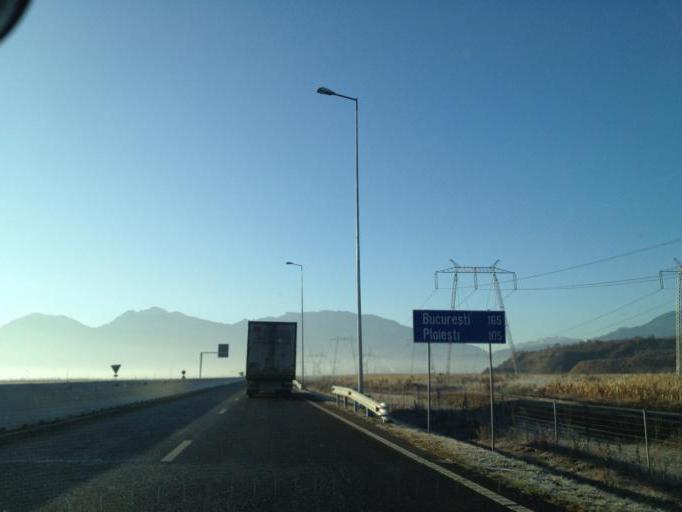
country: RO
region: Brasov
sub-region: Municipiul Sacele
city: Sacele
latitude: 45.6482
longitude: 25.6637
